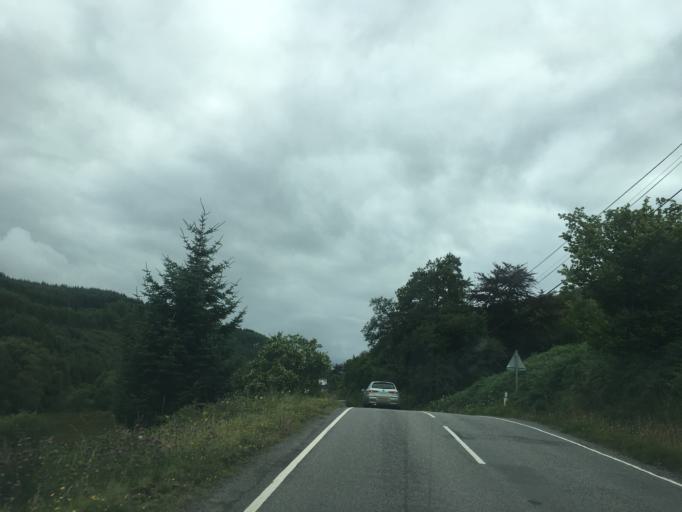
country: GB
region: Scotland
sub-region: Argyll and Bute
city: Oban
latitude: 56.2985
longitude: -5.4635
